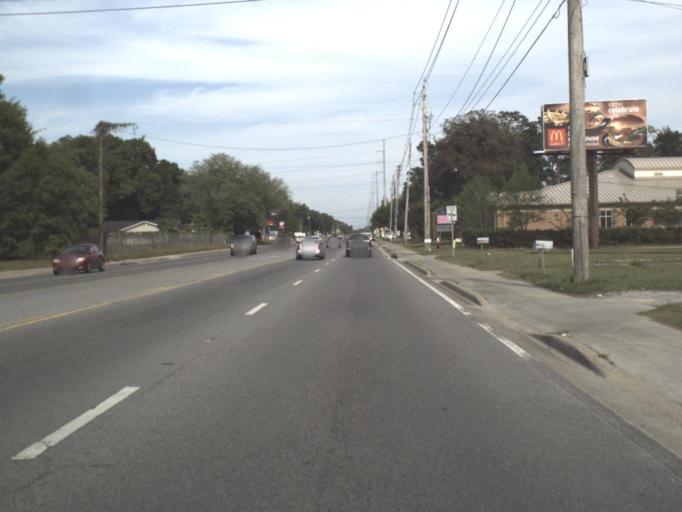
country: US
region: Florida
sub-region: Escambia County
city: Ferry Pass
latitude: 30.4955
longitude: -87.2079
